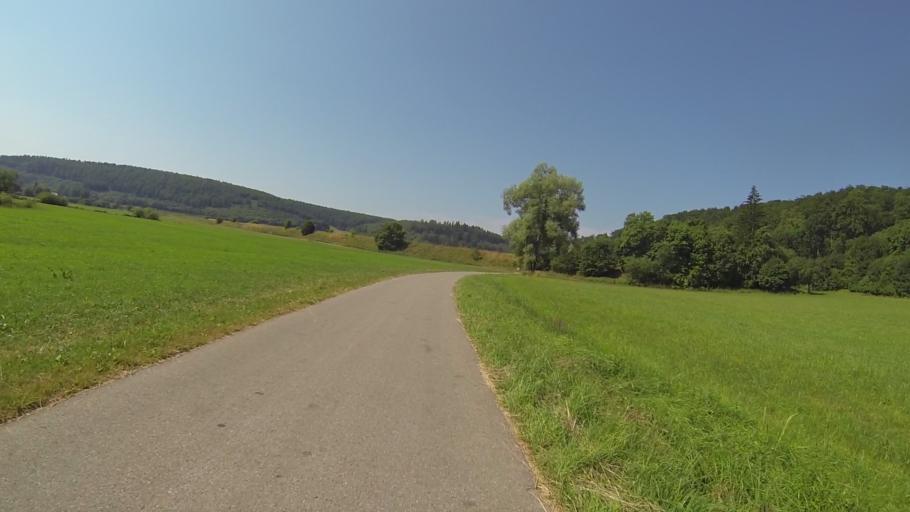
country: DE
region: Baden-Wuerttemberg
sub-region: Regierungsbezirk Stuttgart
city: Konigsbronn
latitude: 48.7243
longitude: 10.1506
